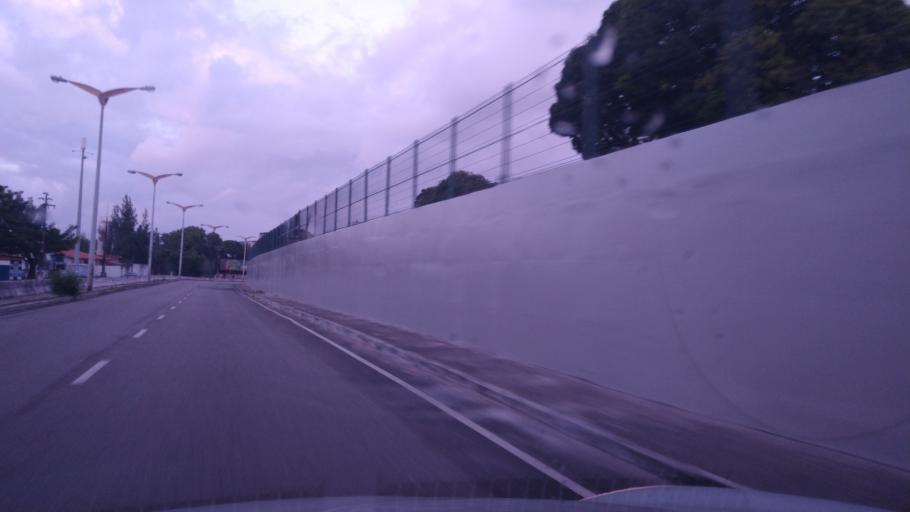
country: BR
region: Ceara
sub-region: Fortaleza
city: Fortaleza
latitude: -3.7496
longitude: -38.4941
